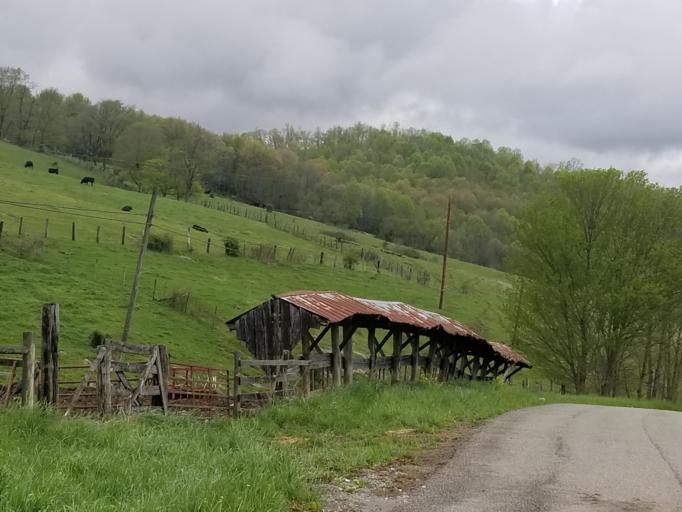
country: US
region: Virginia
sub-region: Smyth County
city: Marion
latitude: 36.9396
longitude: -81.5029
